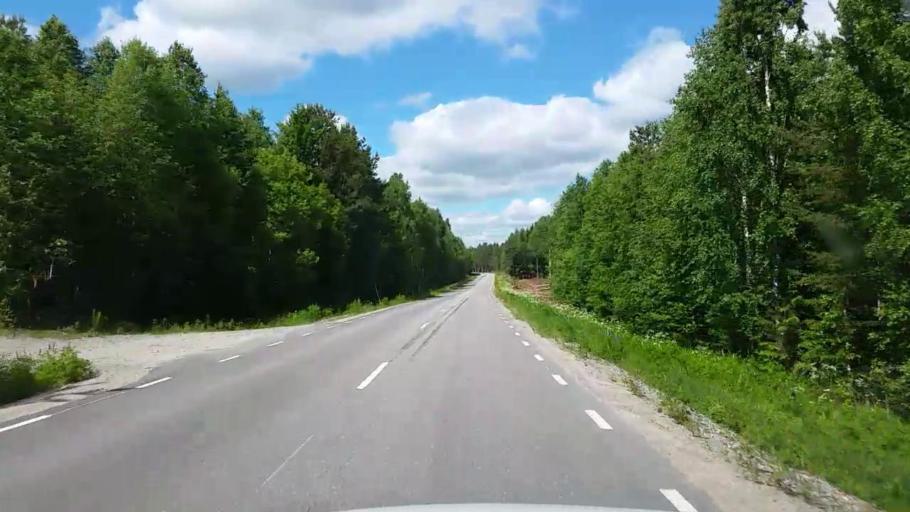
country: SE
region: Gaevleborg
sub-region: Ovanakers Kommun
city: Alfta
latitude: 61.2687
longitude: 16.1177
